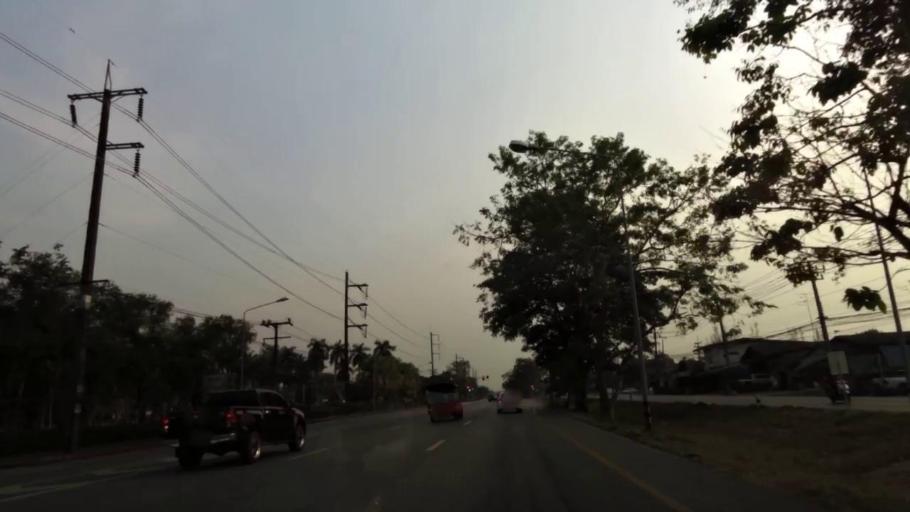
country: TH
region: Chanthaburi
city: Khlung
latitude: 12.5118
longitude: 102.1691
